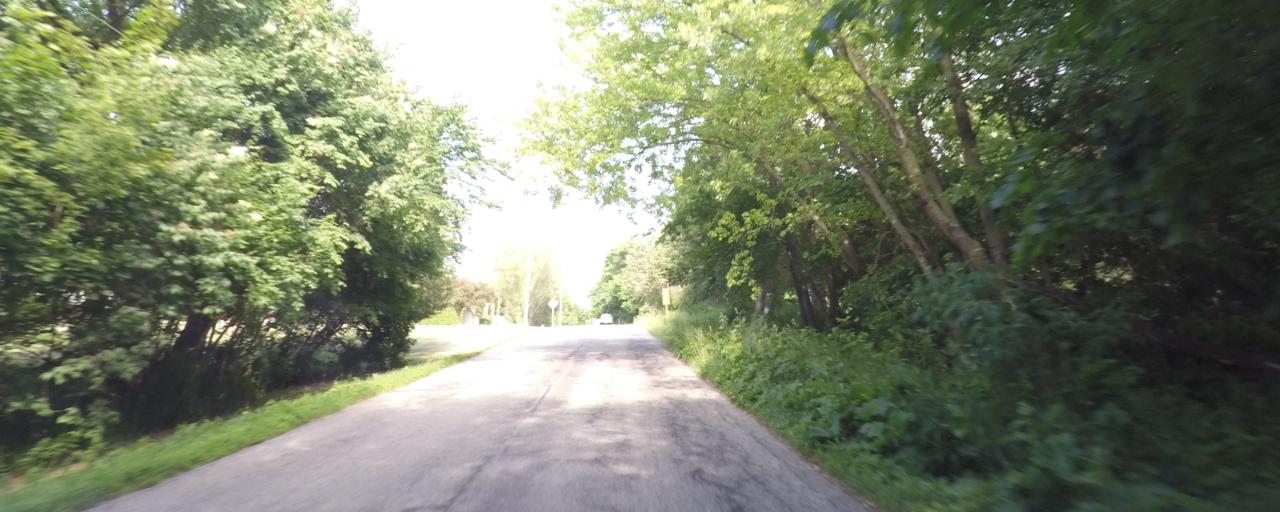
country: US
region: Wisconsin
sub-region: Walworth County
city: Elkhorn
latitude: 42.7640
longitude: -88.5525
